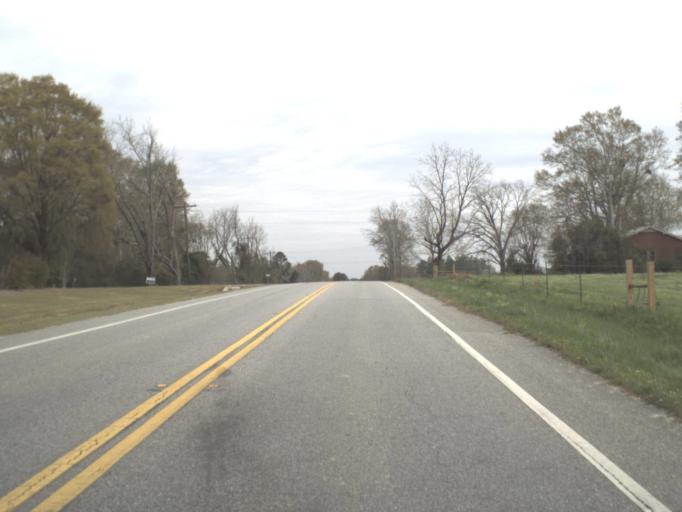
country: US
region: Florida
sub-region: Jackson County
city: Graceville
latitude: 30.9532
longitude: -85.6487
